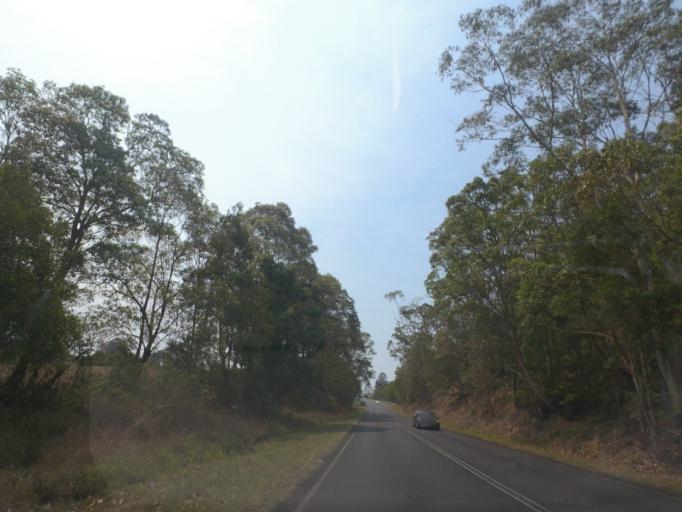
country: AU
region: New South Wales
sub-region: Byron Shire
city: Brunswick Heads
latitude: -28.4958
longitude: 153.5263
